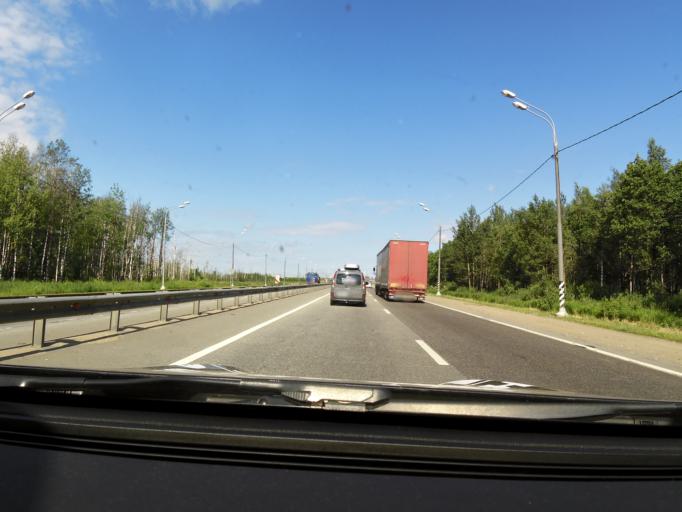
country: RU
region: Tverskaya
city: Tver
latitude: 56.7962
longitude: 35.8729
